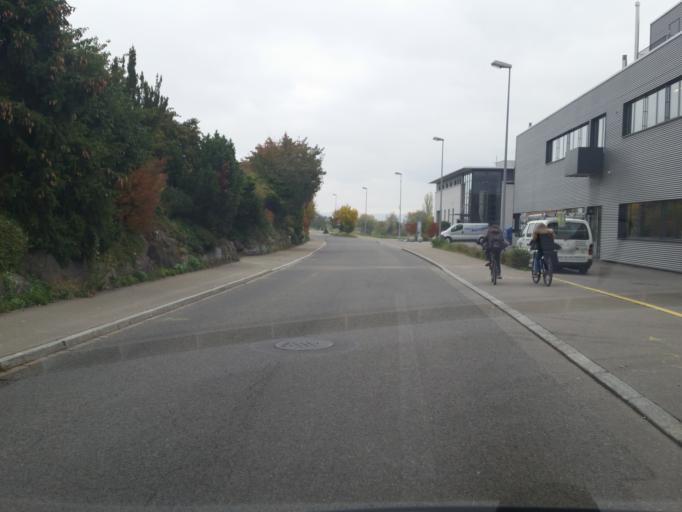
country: CH
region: Zurich
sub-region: Bezirk Dietikon
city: Geroldswil
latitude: 47.4188
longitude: 8.4170
